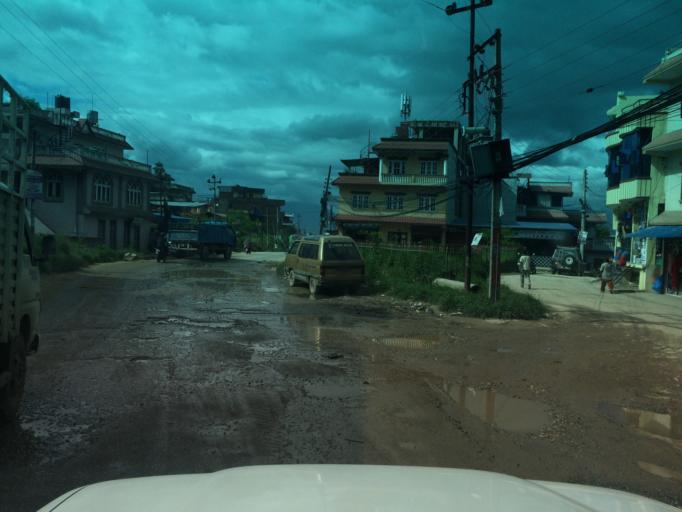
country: NP
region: Central Region
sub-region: Bagmati Zone
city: Patan
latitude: 27.6423
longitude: 85.3047
